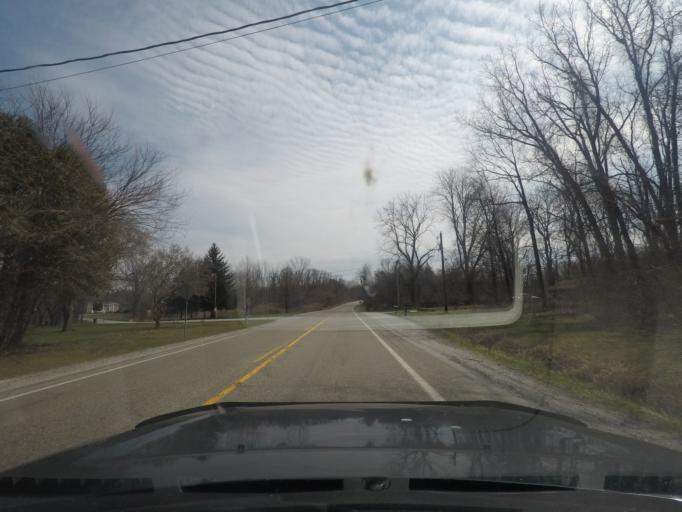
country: US
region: Indiana
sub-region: LaPorte County
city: Trail Creek
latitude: 41.6827
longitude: -86.7919
